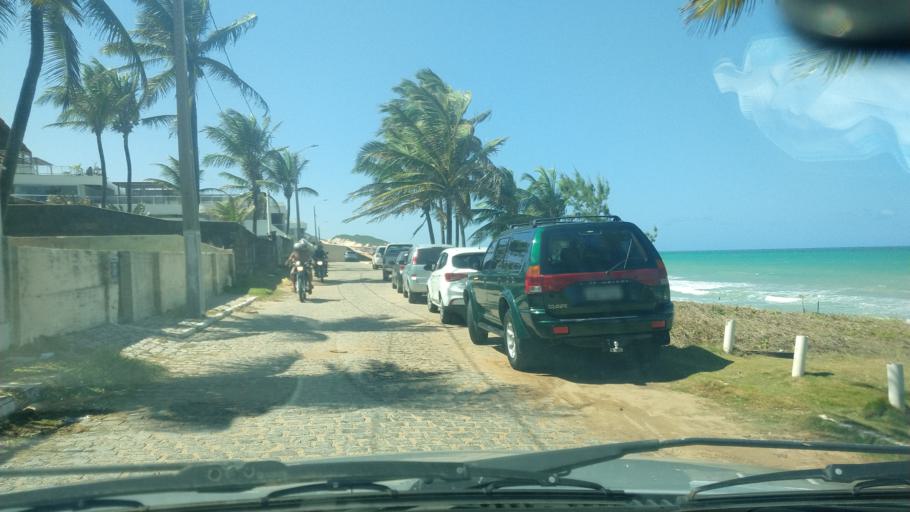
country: BR
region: Rio Grande do Norte
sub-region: Parnamirim
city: Parnamirim
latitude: -5.9482
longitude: -35.1534
